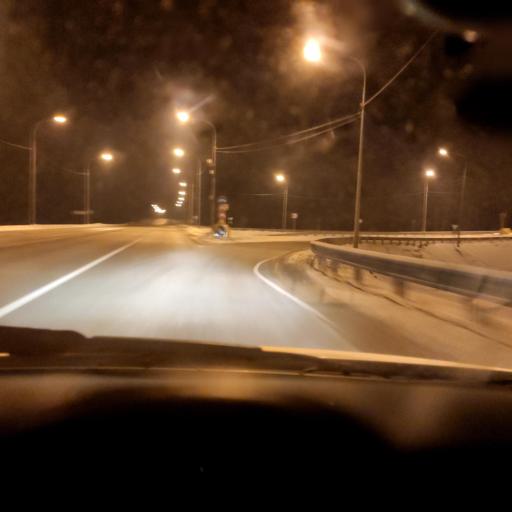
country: RU
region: Kursk
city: Fatezh
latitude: 52.0986
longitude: 35.8217
